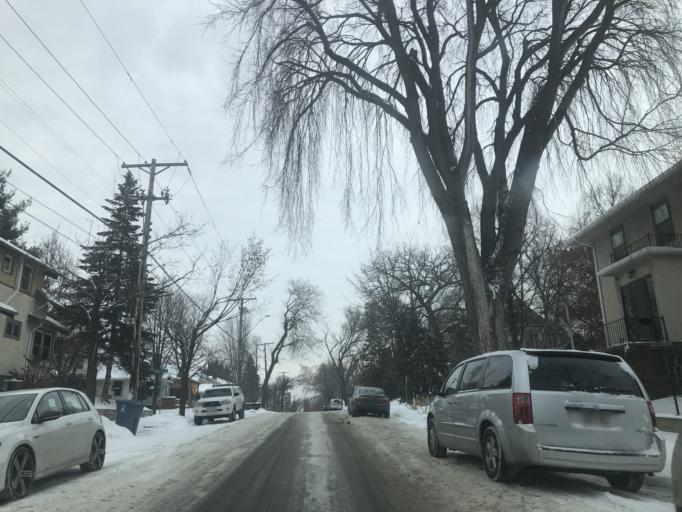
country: US
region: Minnesota
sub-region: Hennepin County
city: Richfield
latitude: 44.9160
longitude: -93.2838
